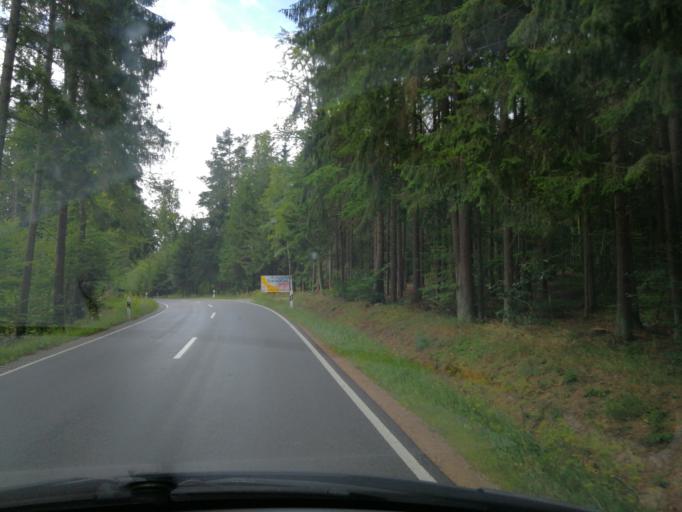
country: DE
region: Bavaria
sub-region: Upper Palatinate
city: Wiesent
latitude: 49.0431
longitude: 12.3685
